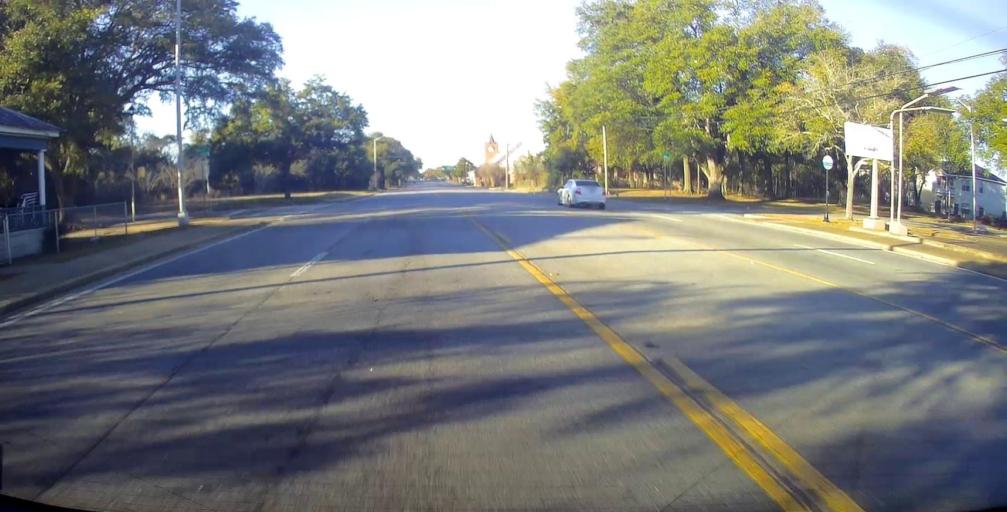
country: US
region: Georgia
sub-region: Dougherty County
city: Albany
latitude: 31.5704
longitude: -84.1560
